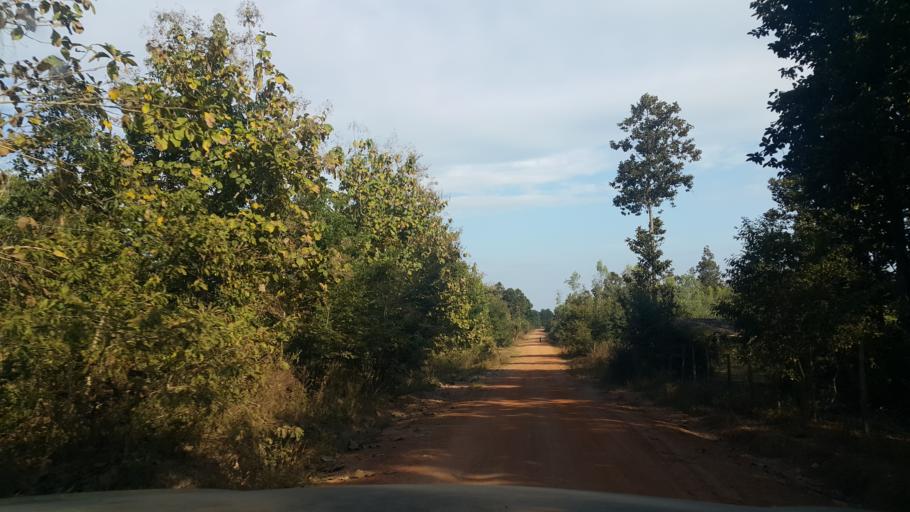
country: TH
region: Lampang
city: Hang Chat
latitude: 18.2923
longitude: 99.3558
